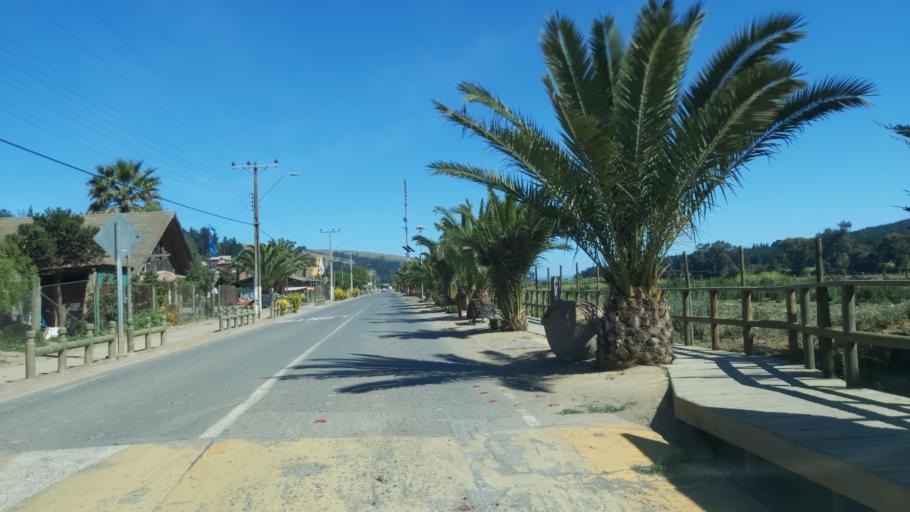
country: CL
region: Maule
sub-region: Provincia de Talca
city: Constitucion
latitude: -34.7690
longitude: -72.0705
